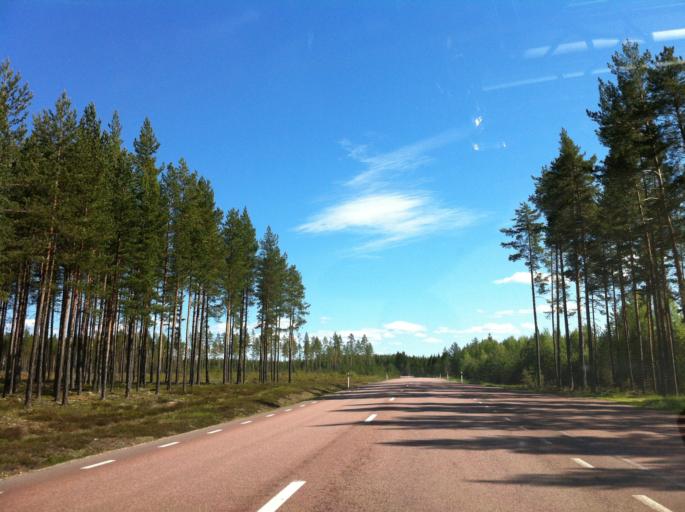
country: SE
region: Dalarna
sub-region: Mora Kommun
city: Mora
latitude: 60.9596
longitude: 14.7183
